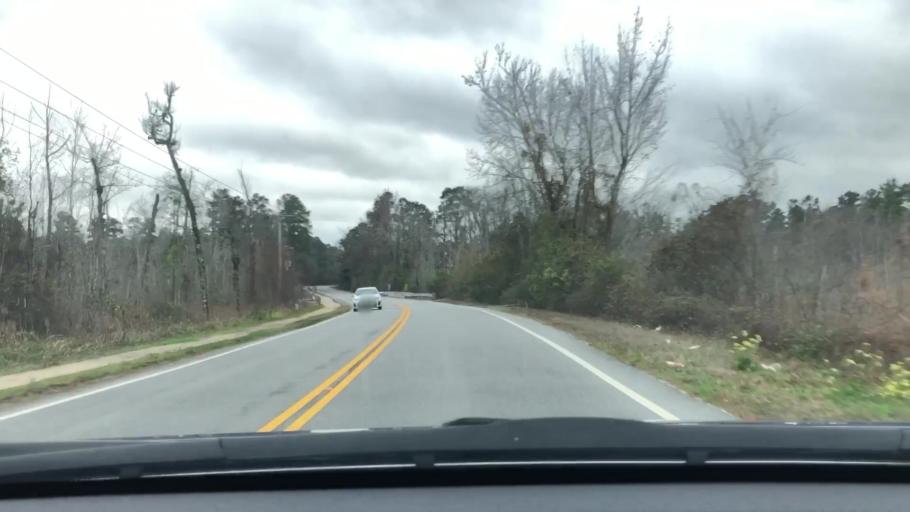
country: US
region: South Carolina
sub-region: Sumter County
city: Cherryvale
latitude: 33.9482
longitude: -80.4030
